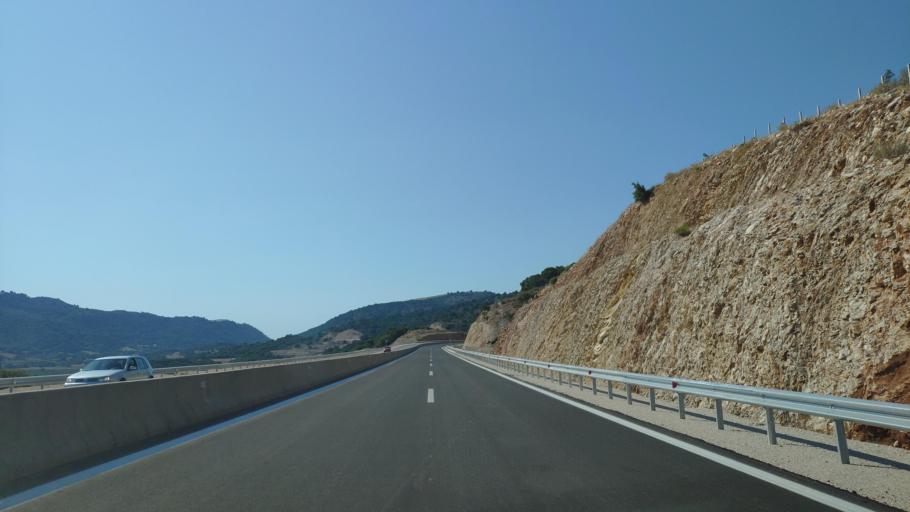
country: GR
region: West Greece
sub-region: Nomos Aitolias kai Akarnanias
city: Katouna
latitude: 38.8310
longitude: 21.1188
